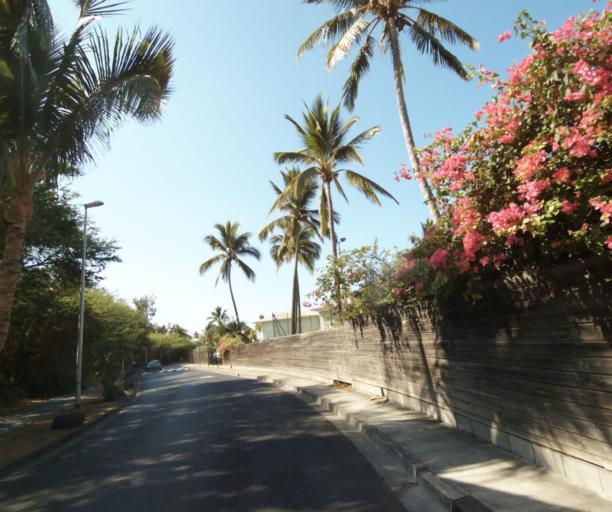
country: RE
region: Reunion
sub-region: Reunion
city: Saint-Paul
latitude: -21.0653
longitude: 55.2223
